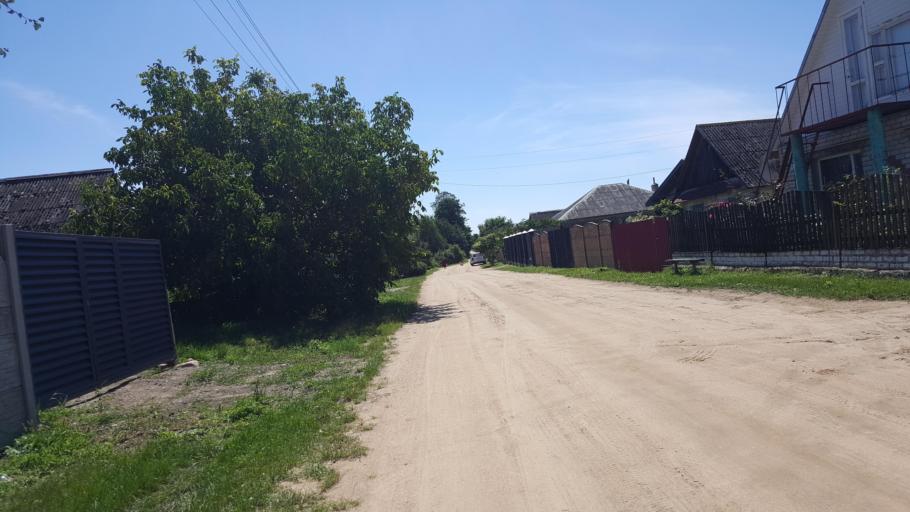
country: BY
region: Brest
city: Charnawchytsy
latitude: 52.2296
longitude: 23.7798
